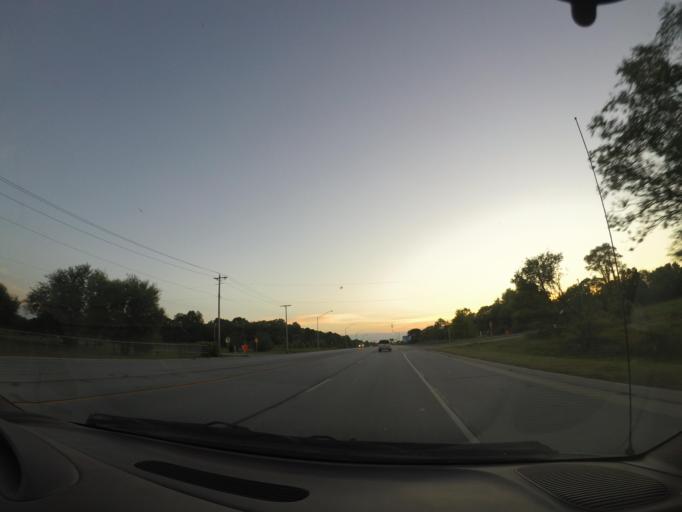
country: US
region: Indiana
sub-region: Elkhart County
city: Dunlap
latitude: 41.6671
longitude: -85.8683
